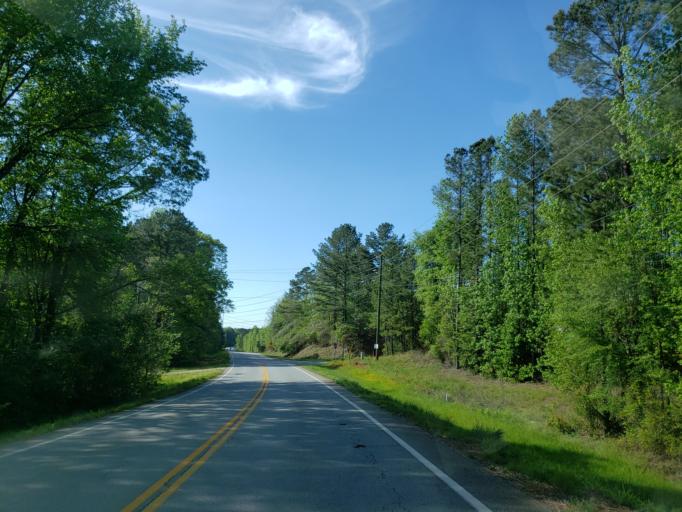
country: US
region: Georgia
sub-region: Haralson County
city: Tallapoosa
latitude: 33.6964
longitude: -85.2633
